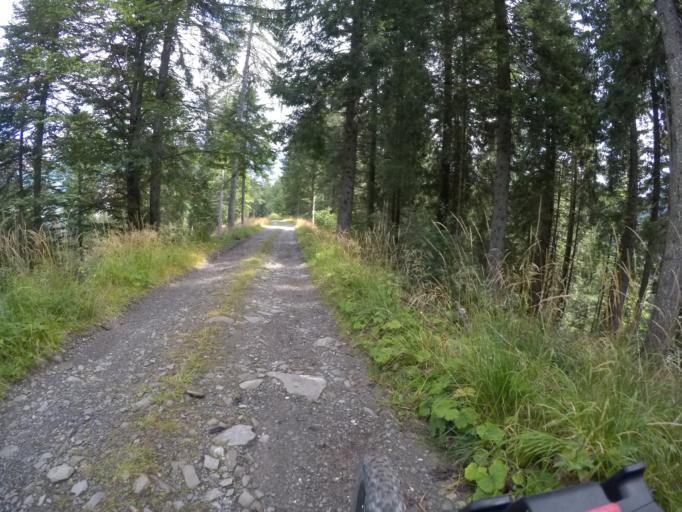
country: IT
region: Friuli Venezia Giulia
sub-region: Provincia di Udine
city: Pontebba
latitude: 46.5157
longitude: 13.2129
